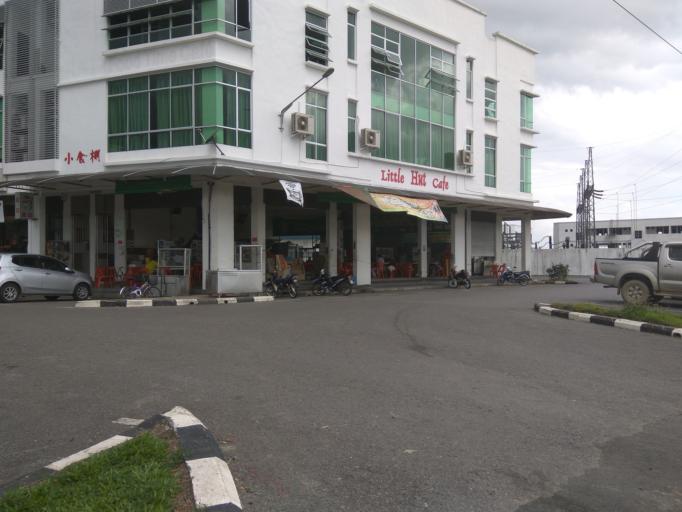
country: MY
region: Sarawak
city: Sibu
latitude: 2.2671
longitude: 111.8615
